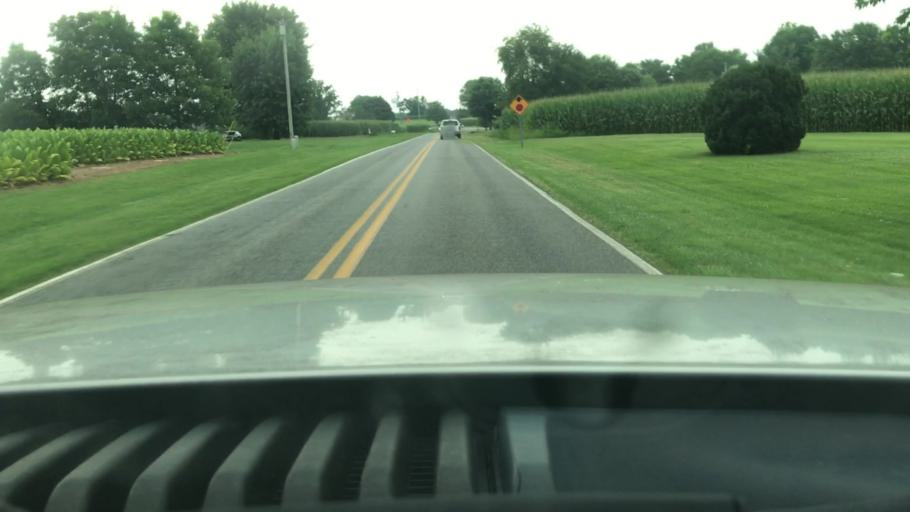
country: US
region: North Carolina
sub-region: Surry County
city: Dobson
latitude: 36.3991
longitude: -80.7989
